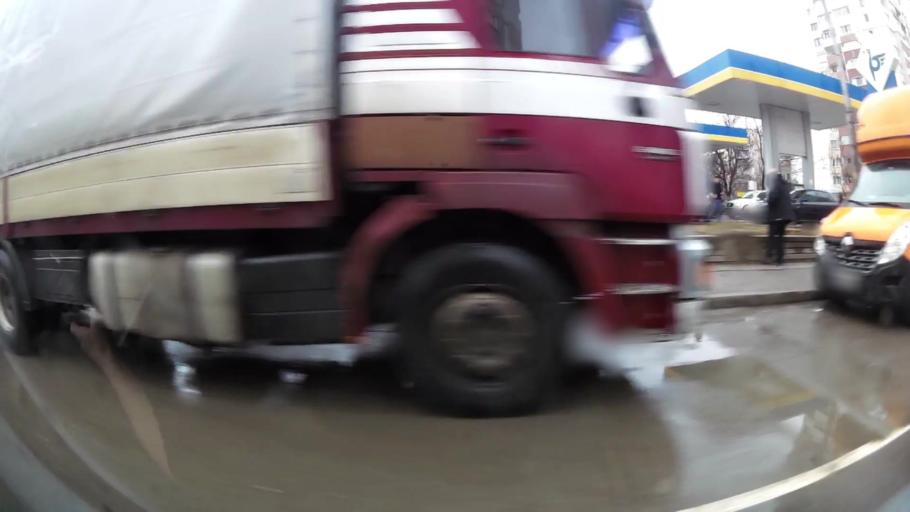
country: BG
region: Sofia-Capital
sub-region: Stolichna Obshtina
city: Sofia
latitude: 42.6390
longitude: 23.3815
